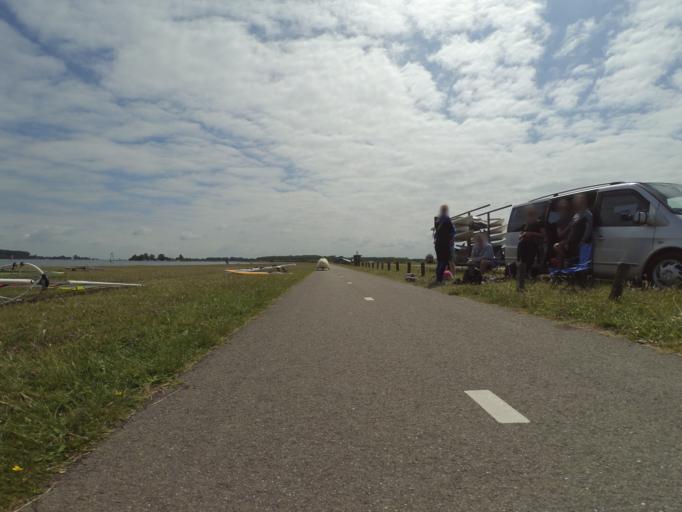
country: NL
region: Zeeland
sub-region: Gemeente Noord-Beveland
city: Kamperland
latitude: 51.5419
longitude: 3.7838
